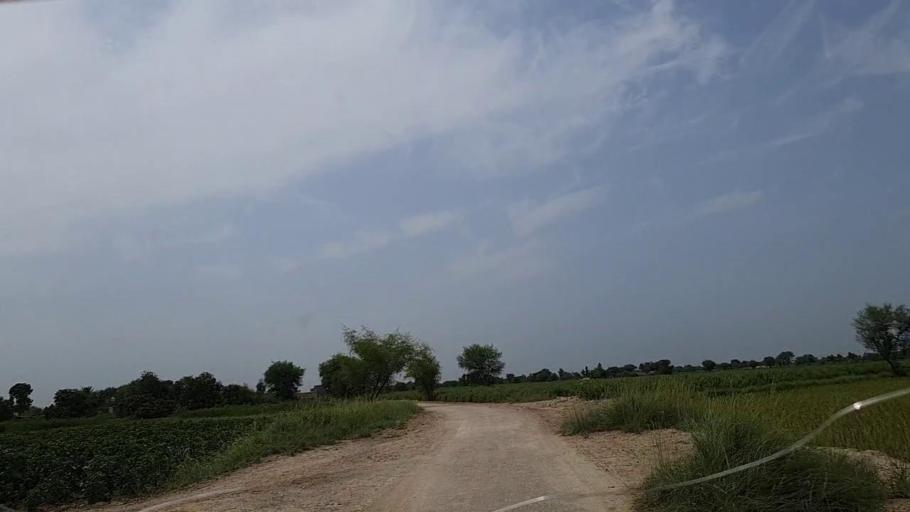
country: PK
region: Sindh
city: Tharu Shah
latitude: 26.8971
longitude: 68.0774
